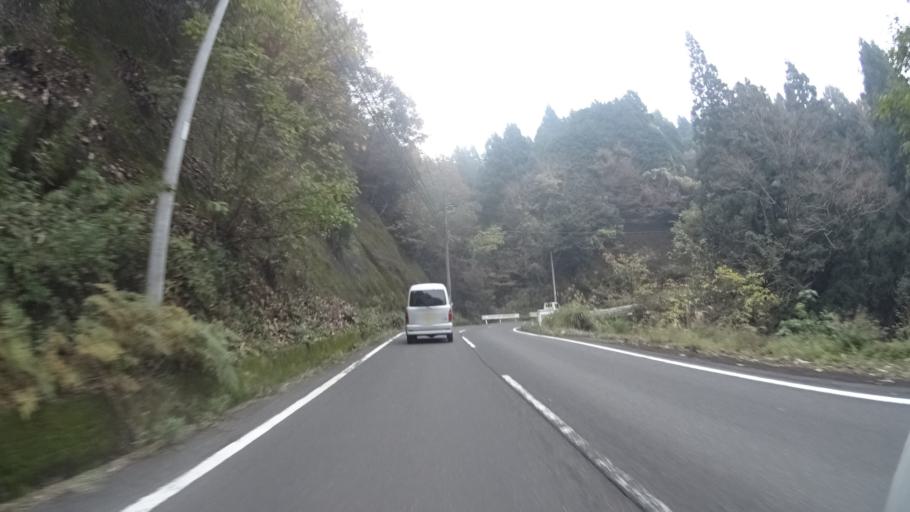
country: JP
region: Kyoto
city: Maizuru
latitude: 35.5354
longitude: 135.4425
